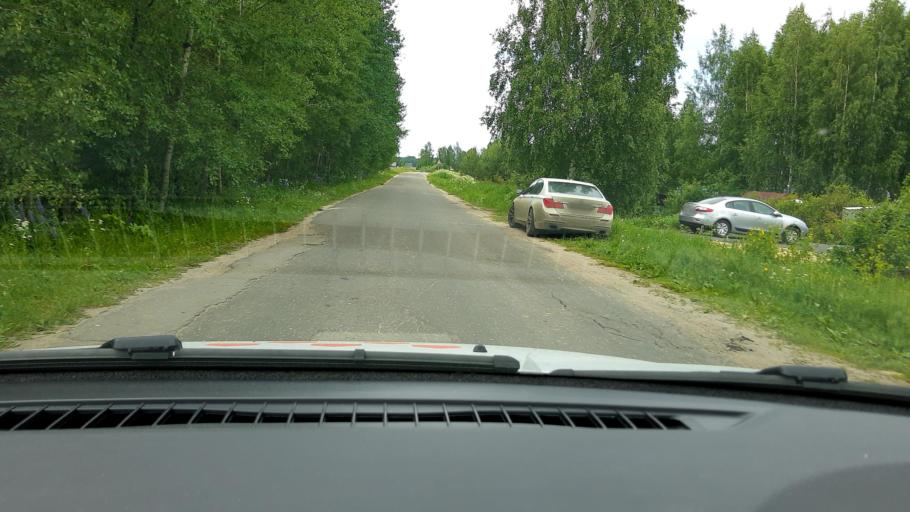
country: RU
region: Nizjnij Novgorod
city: Sitniki
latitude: 56.5239
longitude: 44.1060
